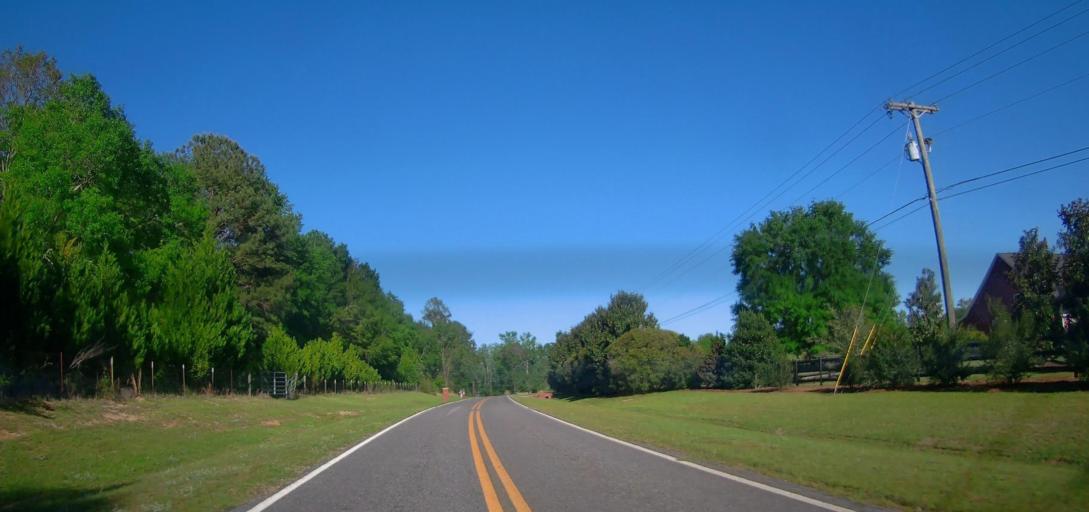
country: US
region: Georgia
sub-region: Houston County
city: Perry
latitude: 32.4643
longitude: -83.8125
